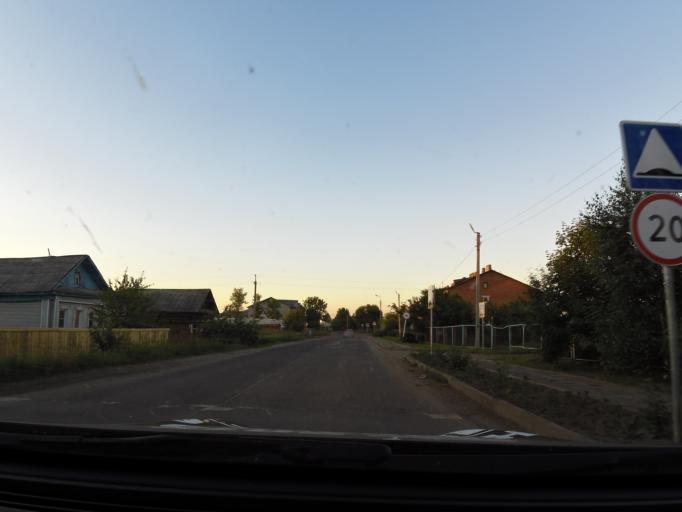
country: RU
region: Jaroslavl
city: Lyubim
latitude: 58.3576
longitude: 40.6959
